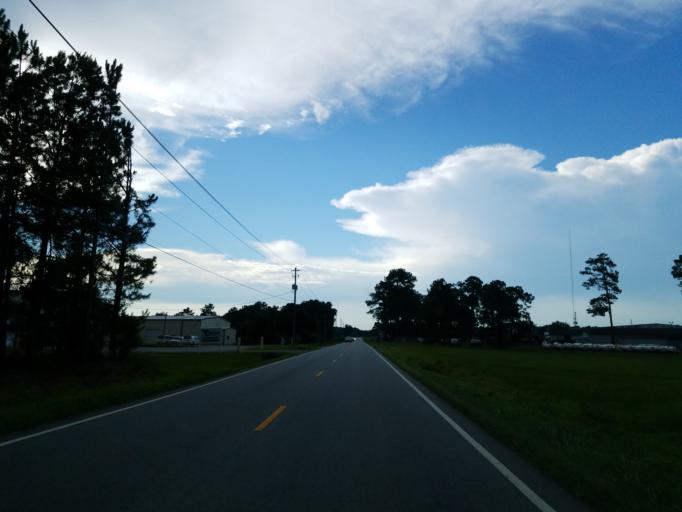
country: US
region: Georgia
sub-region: Tift County
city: Unionville
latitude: 31.4082
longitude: -83.4977
